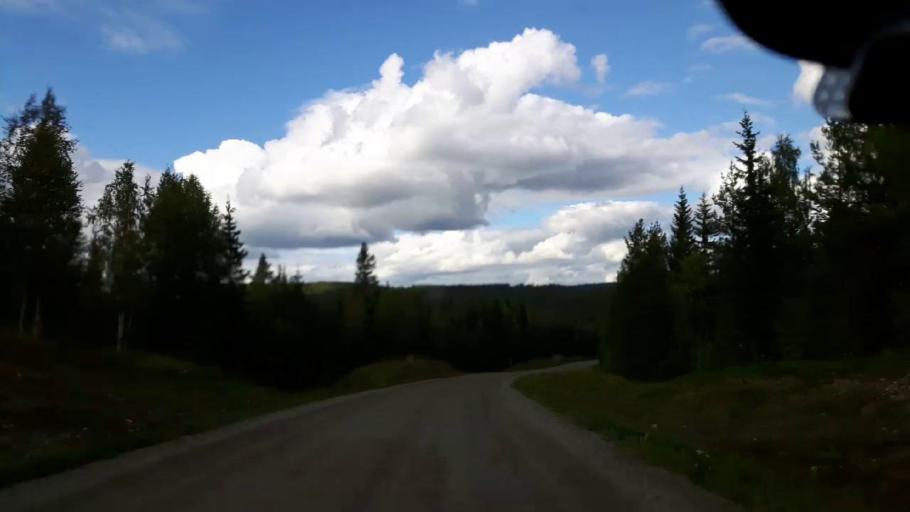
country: SE
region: Jaemtland
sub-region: Stroemsunds Kommun
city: Stroemsund
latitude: 63.4076
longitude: 15.5623
